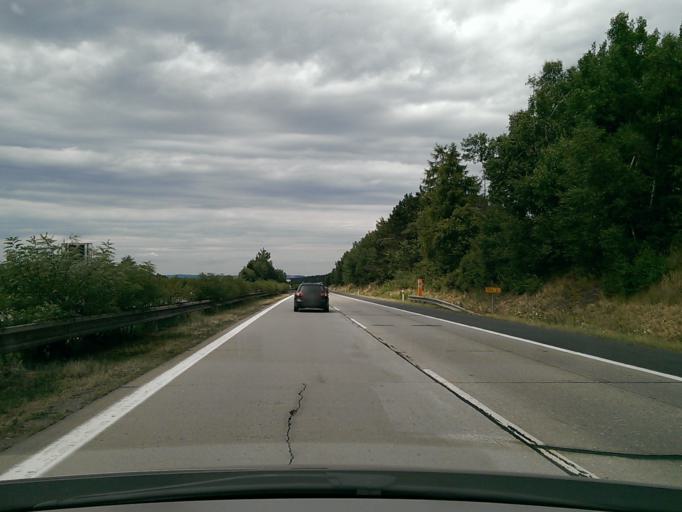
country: CZ
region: Vysocina
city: Kamenice
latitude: 49.4077
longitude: 15.7776
